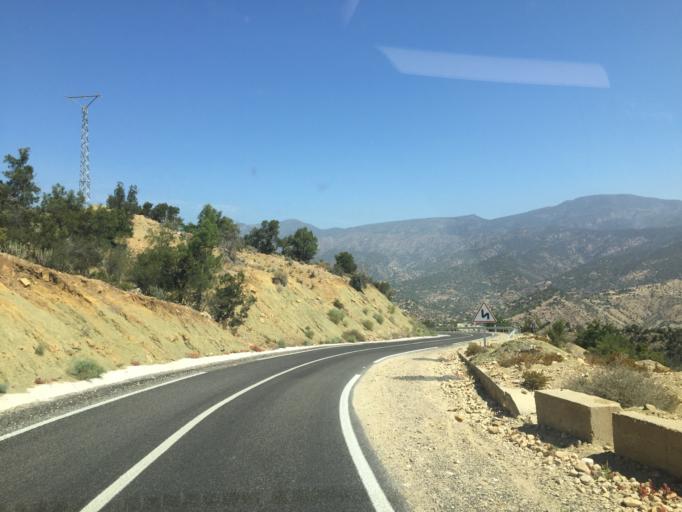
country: MA
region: Souss-Massa-Draa
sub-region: Agadir-Ida-ou-Tnan
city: Aourir
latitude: 30.5441
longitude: -9.5715
